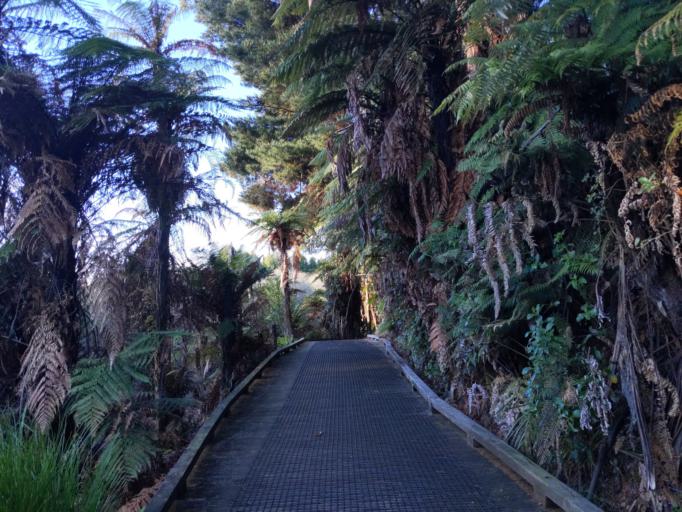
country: NZ
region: Waikato
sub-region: Hamilton City
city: Hamilton
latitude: -37.7385
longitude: 175.2773
